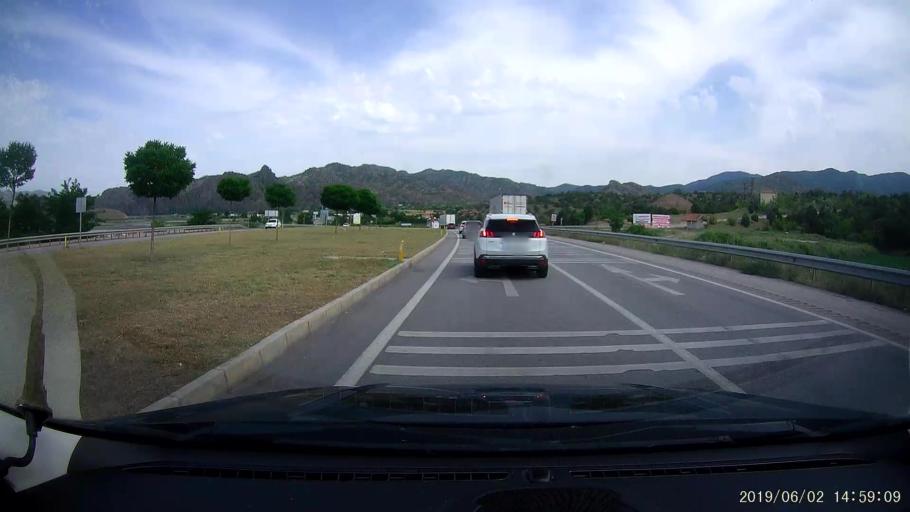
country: TR
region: Corum
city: Osmancik
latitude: 40.9722
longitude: 34.6915
